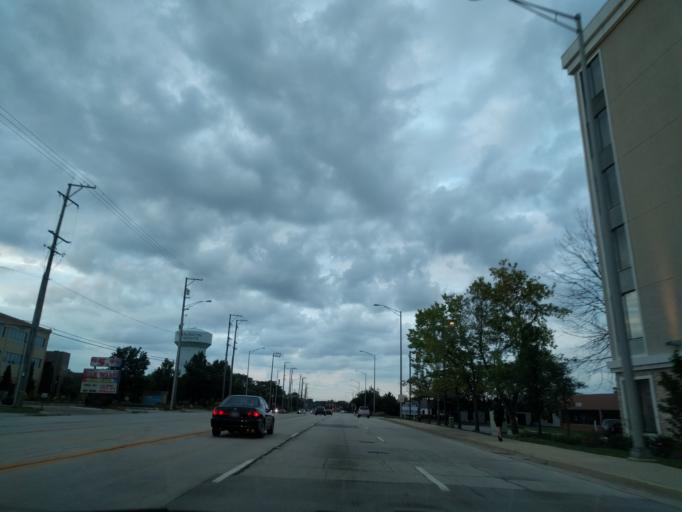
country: US
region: Illinois
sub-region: Cook County
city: Arlington Heights
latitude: 42.0468
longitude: -87.9825
